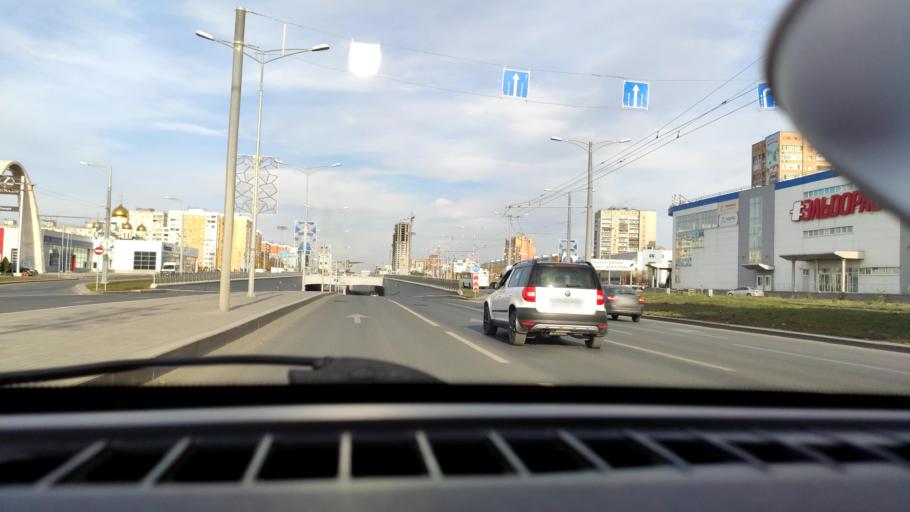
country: RU
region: Samara
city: Samara
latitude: 53.2489
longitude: 50.2190
